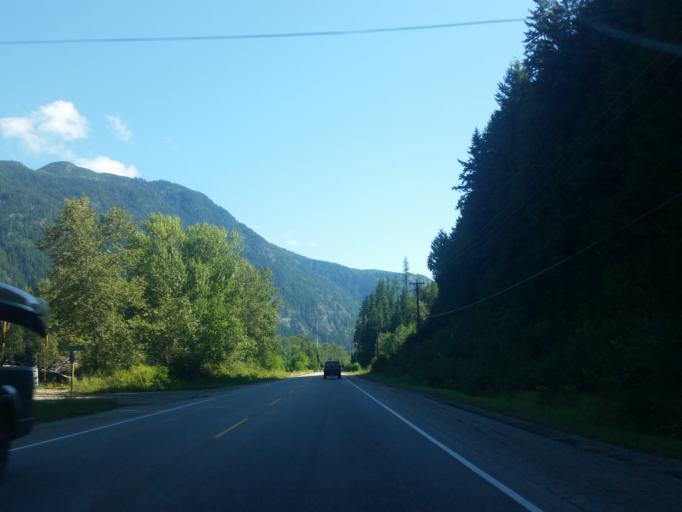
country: CA
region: British Columbia
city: Sicamous
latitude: 50.8790
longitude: -118.9176
